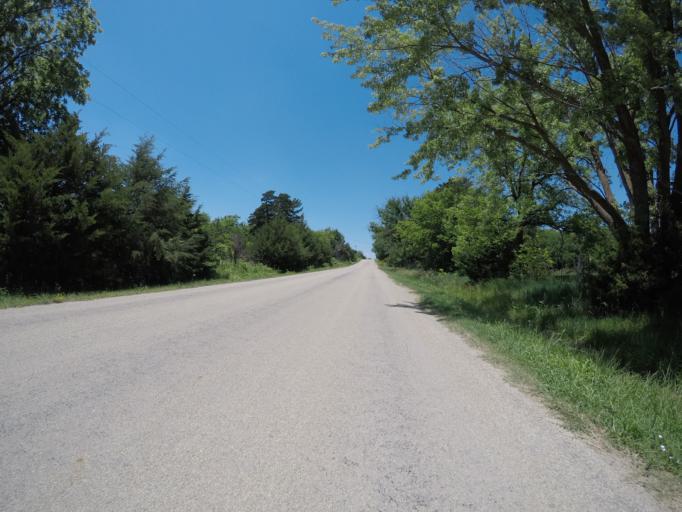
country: US
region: Kansas
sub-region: Geary County
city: Grandview Plaza
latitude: 38.8682
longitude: -96.7944
